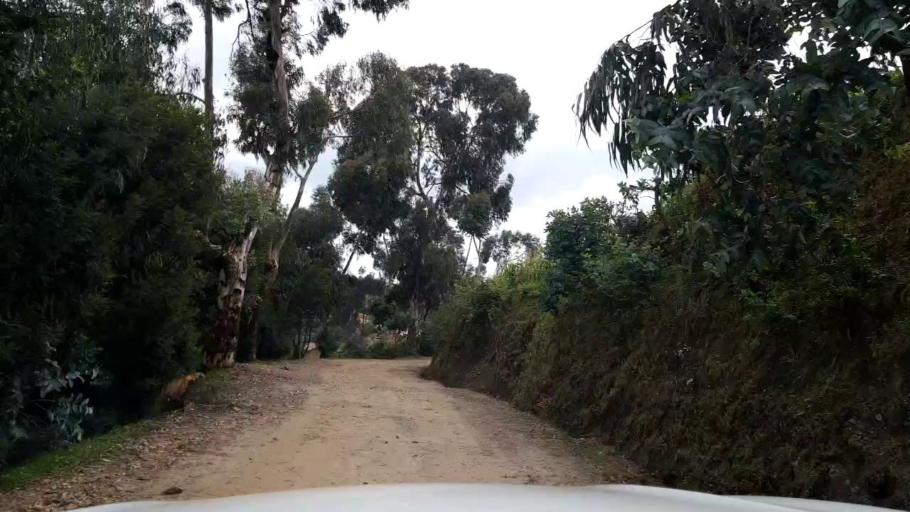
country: RW
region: Western Province
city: Kibuye
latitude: -1.9410
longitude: 29.4672
